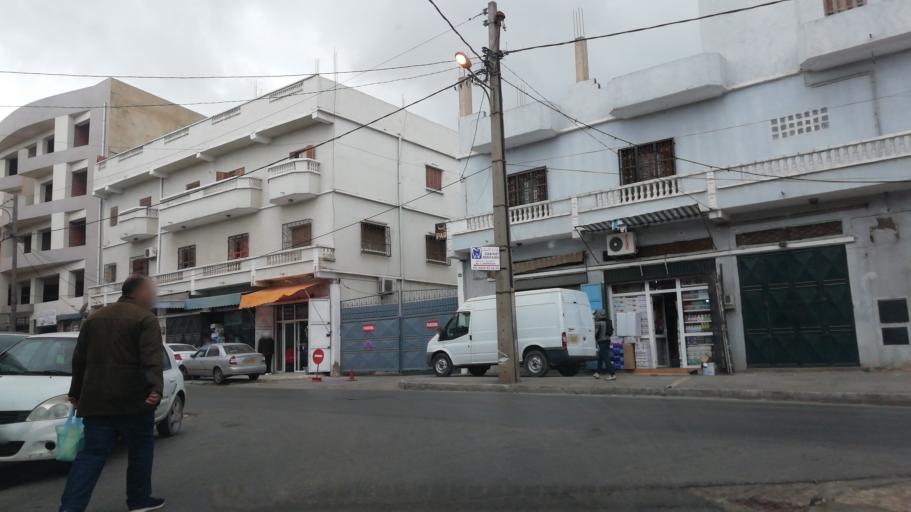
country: DZ
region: Oran
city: Oran
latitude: 35.6877
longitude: -0.6539
